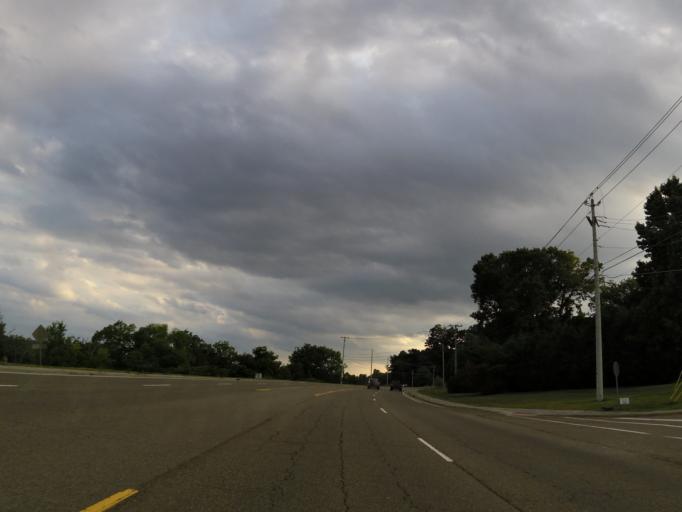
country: US
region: Tennessee
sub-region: Knox County
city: Knoxville
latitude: 36.0721
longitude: -83.9634
